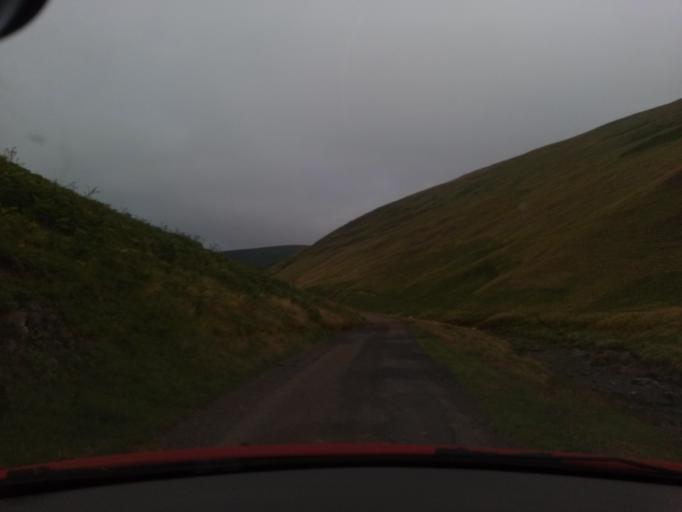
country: GB
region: England
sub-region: Northumberland
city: Rochester
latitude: 55.3961
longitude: -2.2222
